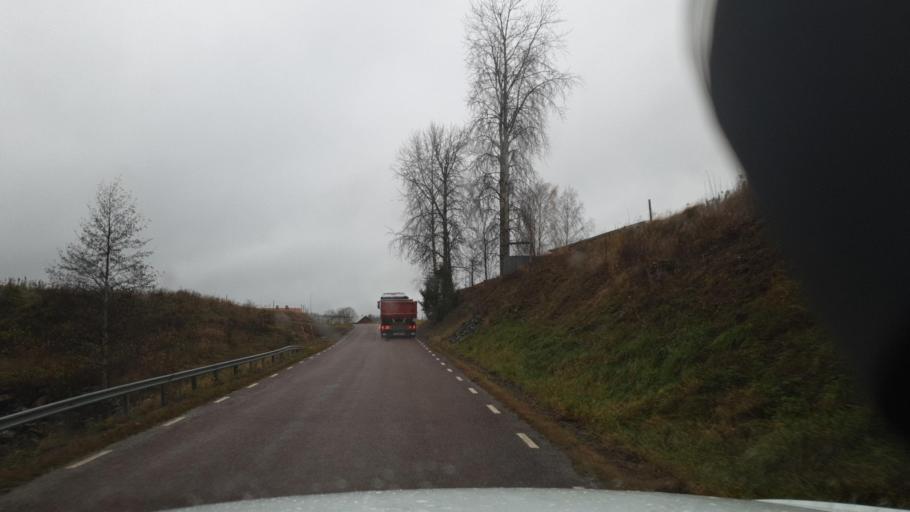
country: SE
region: Vaermland
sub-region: Sunne Kommun
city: Sunne
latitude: 59.7410
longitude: 13.0626
